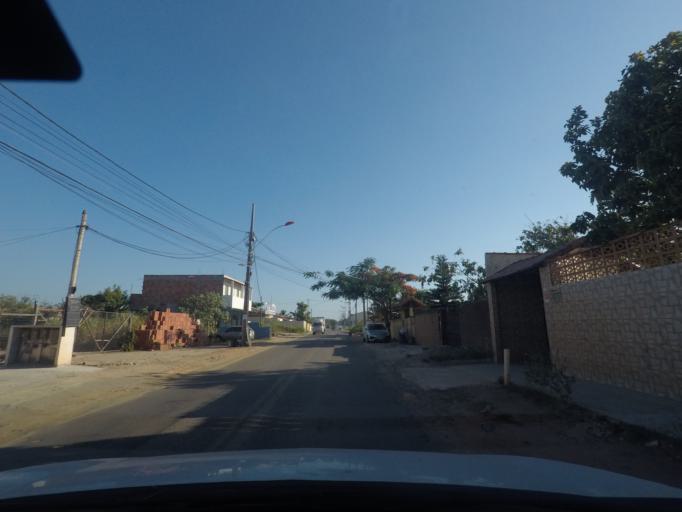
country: BR
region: Rio de Janeiro
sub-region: Marica
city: Marica
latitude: -22.9584
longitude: -42.9425
